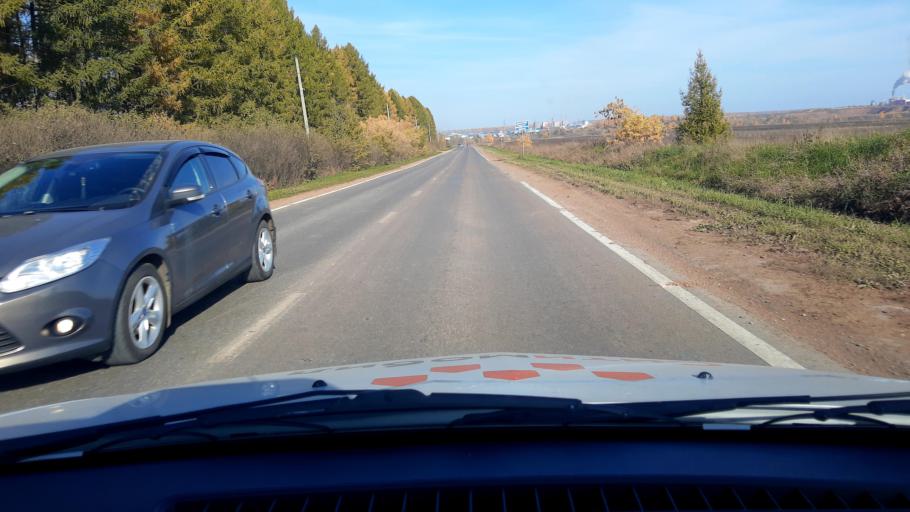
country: RU
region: Bashkortostan
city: Iglino
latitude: 54.7408
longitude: 56.2549
